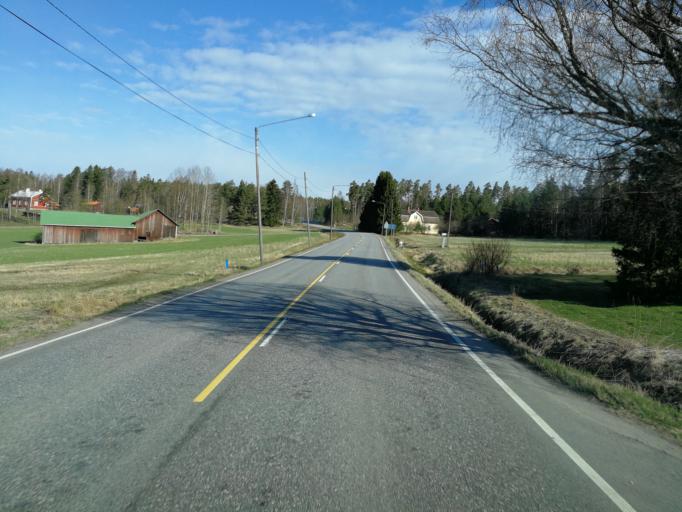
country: FI
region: Uusimaa
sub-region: Helsinki
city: Kirkkonummi
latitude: 60.2219
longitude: 24.4684
